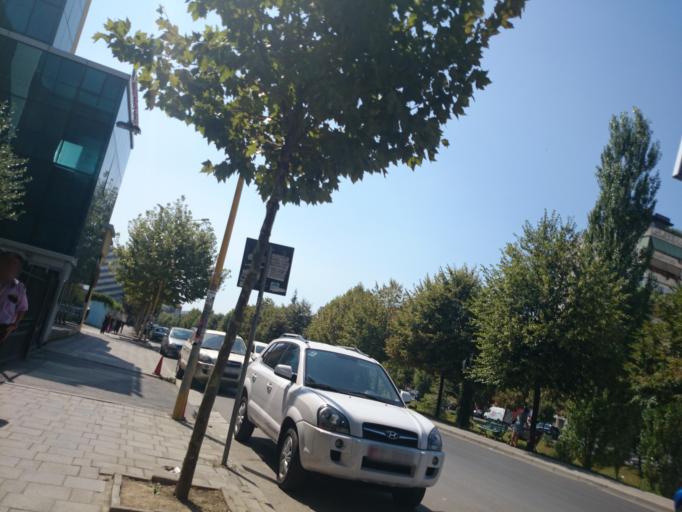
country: AL
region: Tirane
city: Tirana
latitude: 41.3291
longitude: 19.8320
